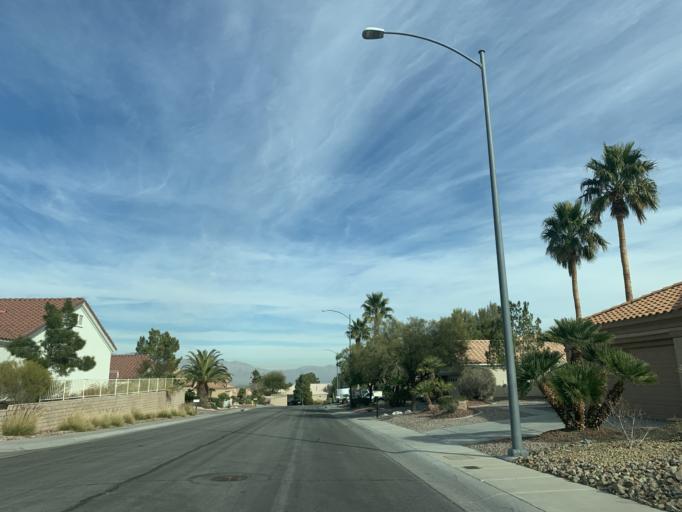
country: US
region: Nevada
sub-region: Clark County
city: Summerlin South
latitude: 36.2165
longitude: -115.3242
